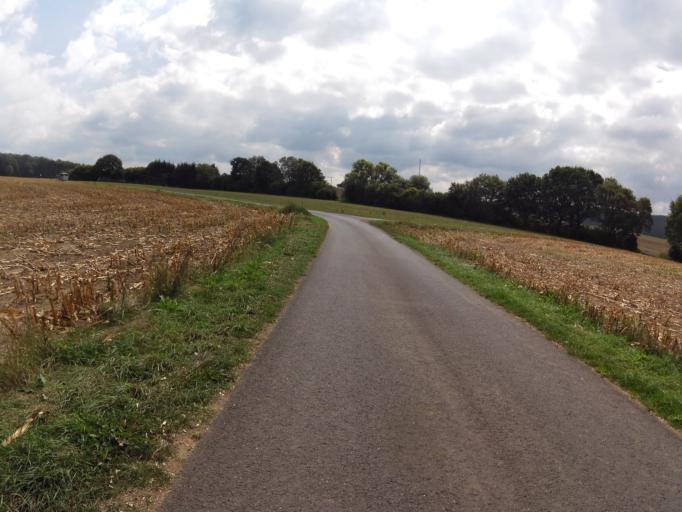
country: DE
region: Rheinland-Pfalz
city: Oberbettingen
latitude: 50.2775
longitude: 6.6497
